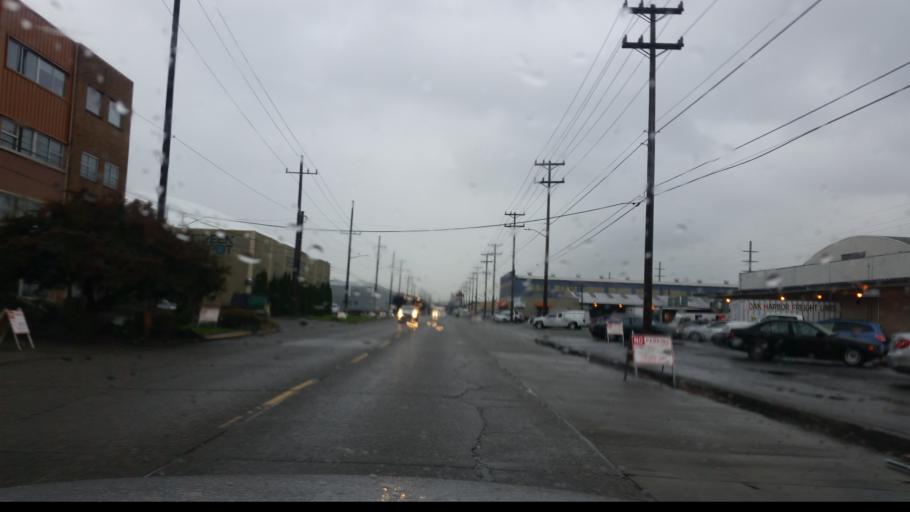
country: US
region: Washington
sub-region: King County
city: Seattle
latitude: 47.5853
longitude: -122.3260
